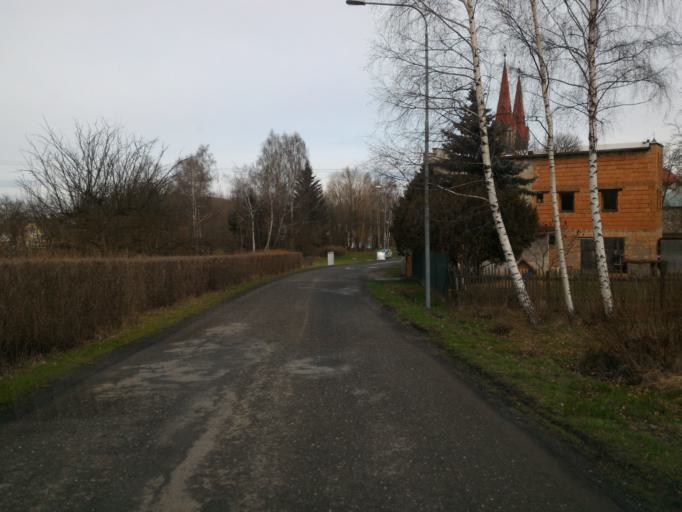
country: DE
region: Saxony
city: Neugersdorf
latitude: 50.9791
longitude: 14.5966
